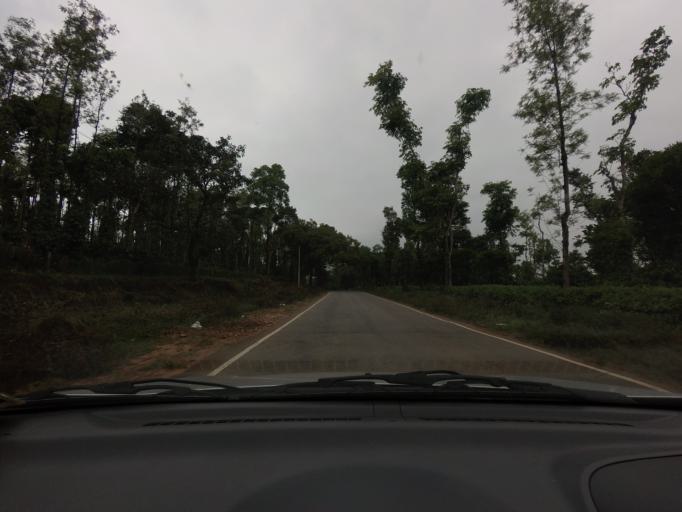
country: IN
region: Karnataka
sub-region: Hassan
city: Sakleshpur
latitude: 12.9382
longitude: 75.7616
